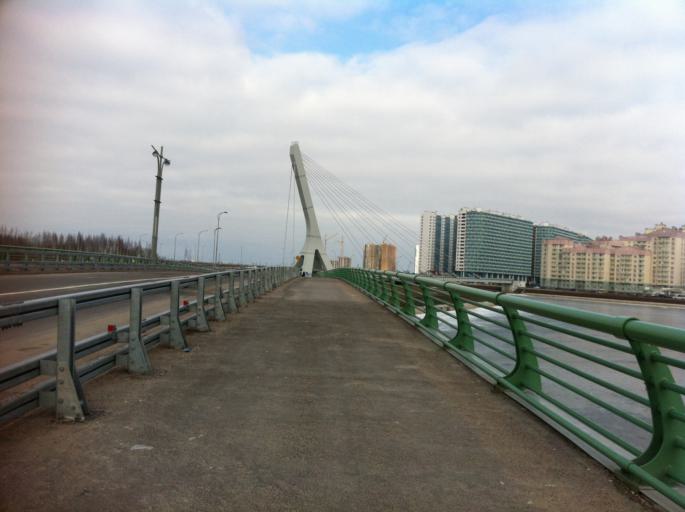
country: RU
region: St.-Petersburg
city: Sosnovaya Polyana
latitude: 59.8558
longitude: 30.1560
